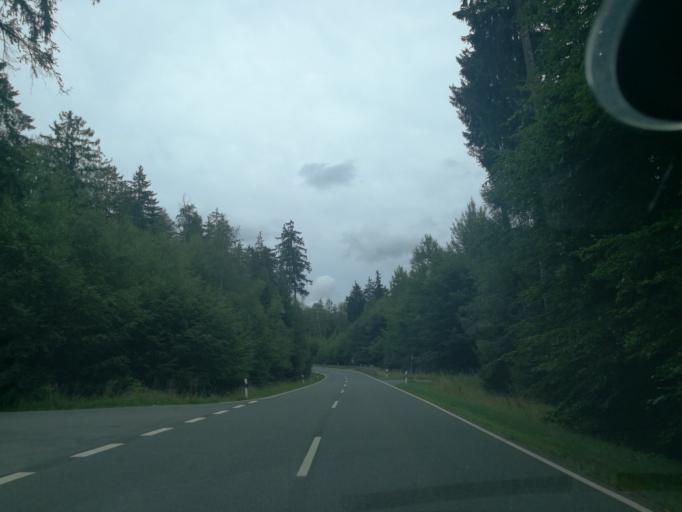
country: DE
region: Saxony
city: Eichigt
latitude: 50.3357
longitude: 12.1693
